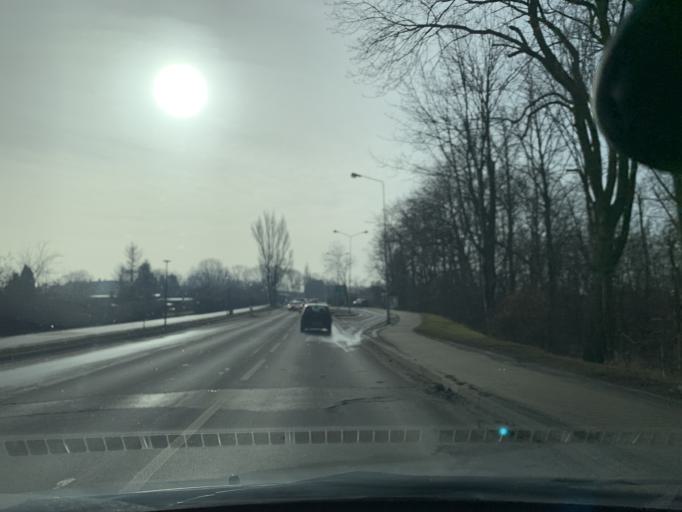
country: PL
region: Silesian Voivodeship
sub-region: Ruda Slaska
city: Ruda Slaska
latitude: 50.3088
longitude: 18.8526
